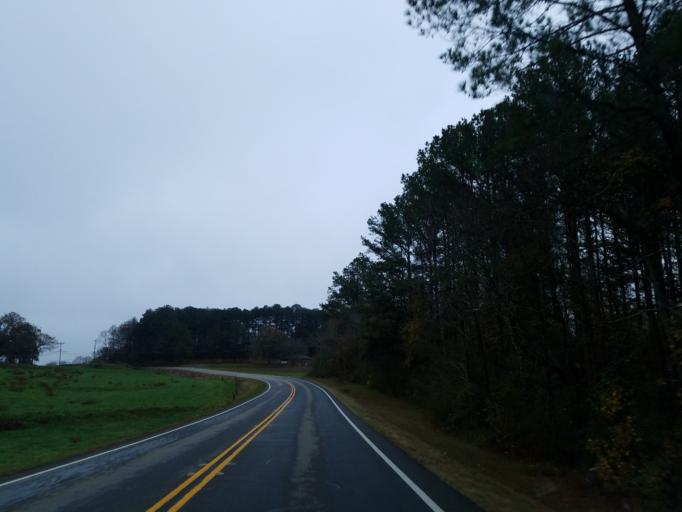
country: US
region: Georgia
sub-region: Pickens County
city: Nelson
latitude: 34.3888
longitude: -84.4440
